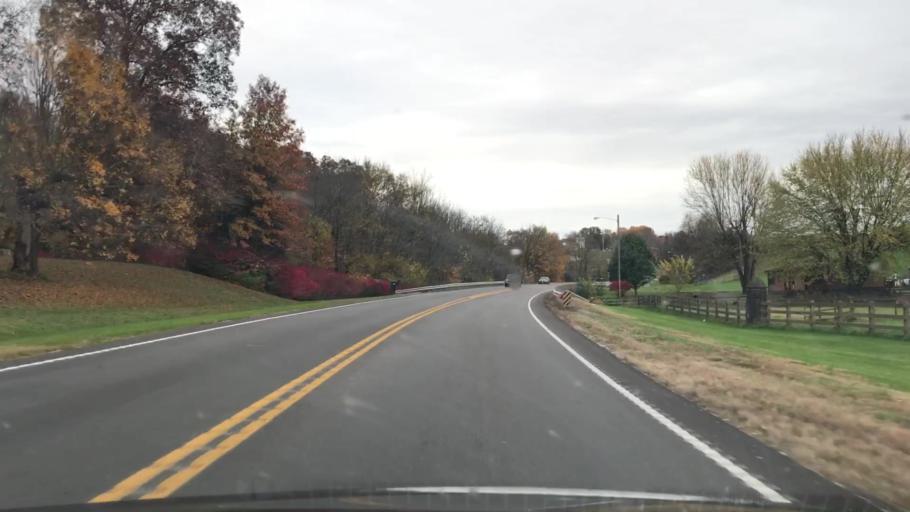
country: US
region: Kentucky
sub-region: Barren County
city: Glasgow
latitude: 37.0253
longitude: -85.9064
